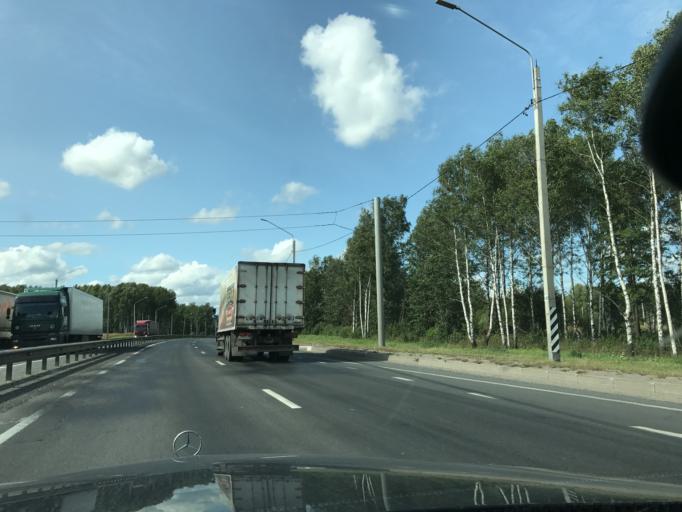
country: RU
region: Vladimir
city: Vyazniki
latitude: 56.2226
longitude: 42.1342
